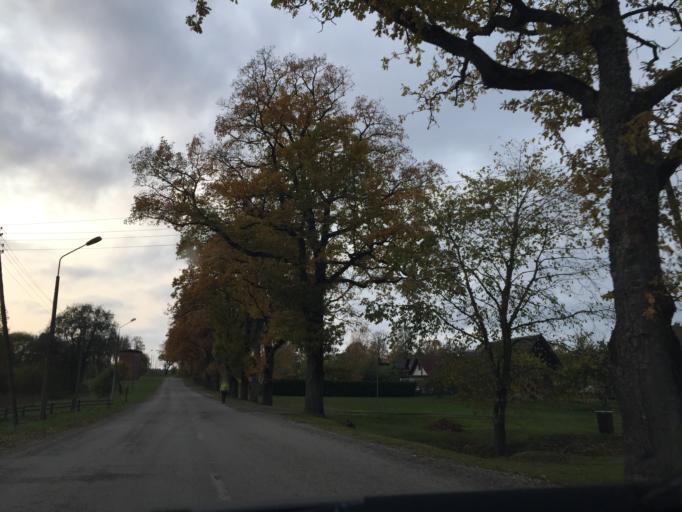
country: LV
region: Pargaujas
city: Stalbe
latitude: 57.3360
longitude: 25.1466
